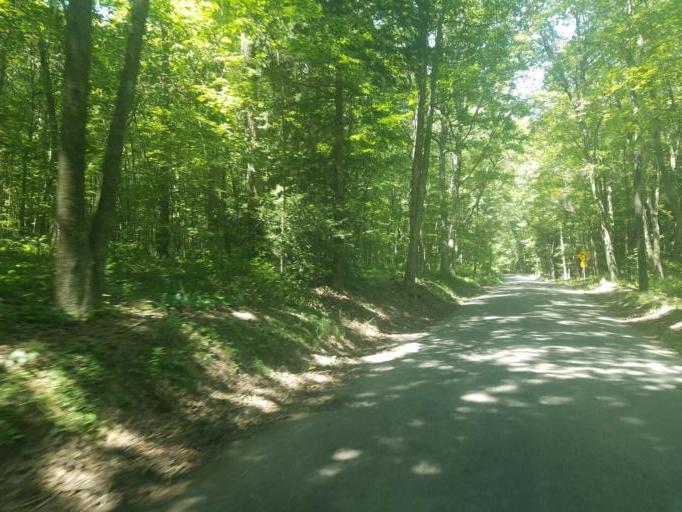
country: US
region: Pennsylvania
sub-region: Clarion County
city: Knox
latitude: 41.1844
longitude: -79.5071
